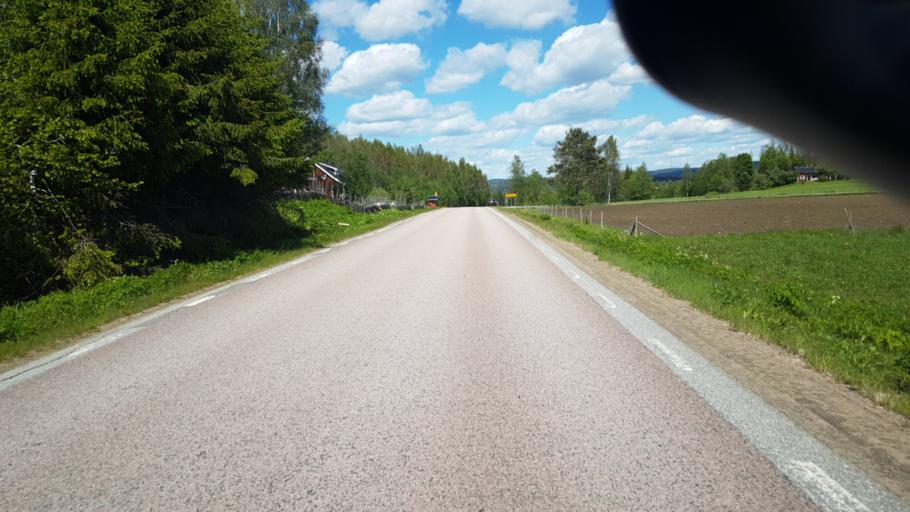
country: SE
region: Vaermland
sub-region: Arvika Kommun
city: Arvika
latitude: 59.7222
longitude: 12.7982
